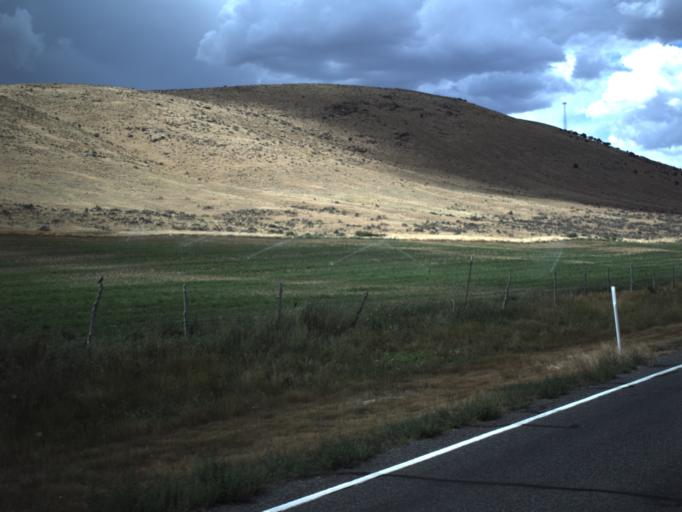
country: US
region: Utah
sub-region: Sanpete County
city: Gunnison
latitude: 39.1446
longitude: -111.7096
